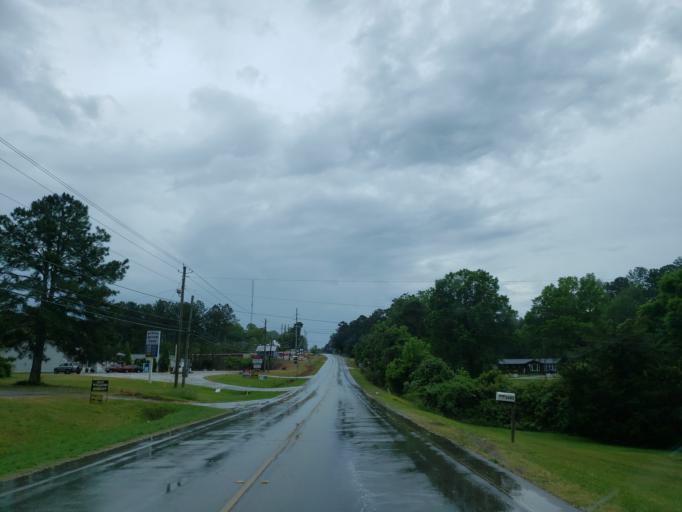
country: US
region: Georgia
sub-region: Haralson County
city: Buchanan
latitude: 33.7960
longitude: -85.1870
